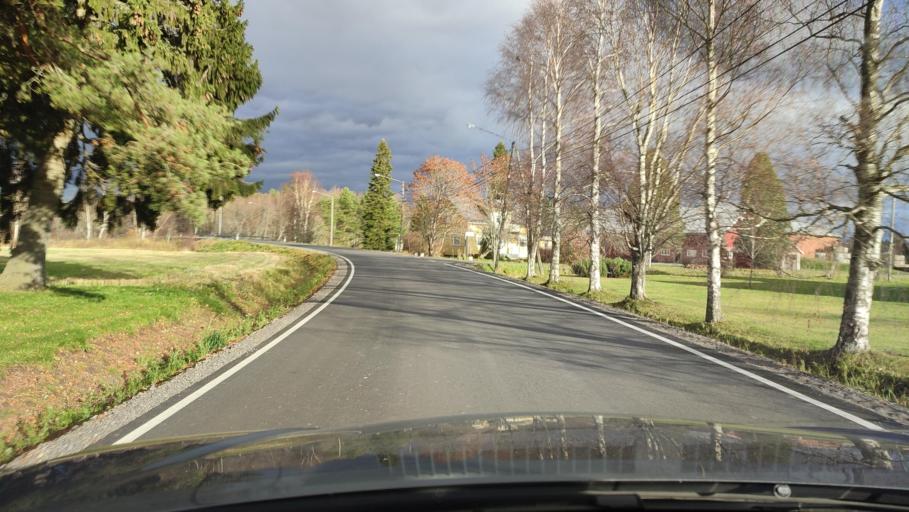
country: FI
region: Southern Ostrobothnia
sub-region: Suupohja
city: Karijoki
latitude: 62.2376
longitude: 21.5759
